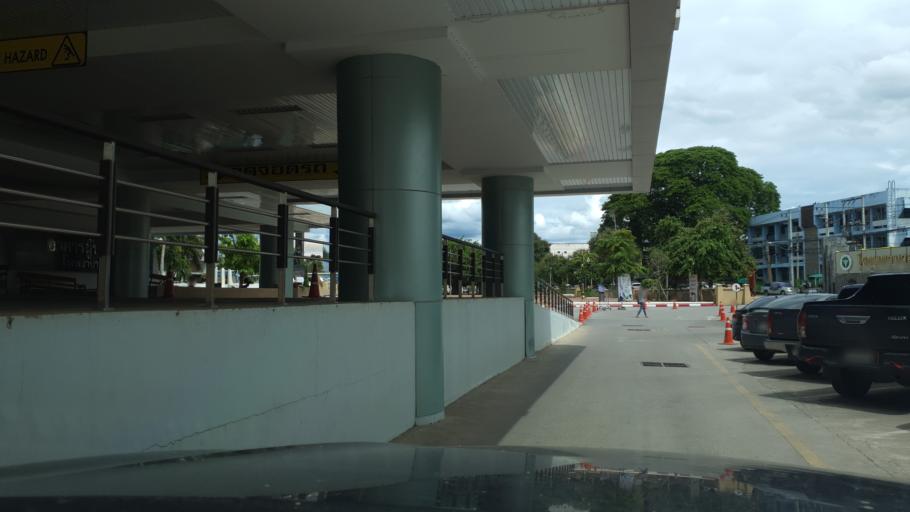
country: TH
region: Lampang
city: Lampang
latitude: 18.2862
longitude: 99.5060
